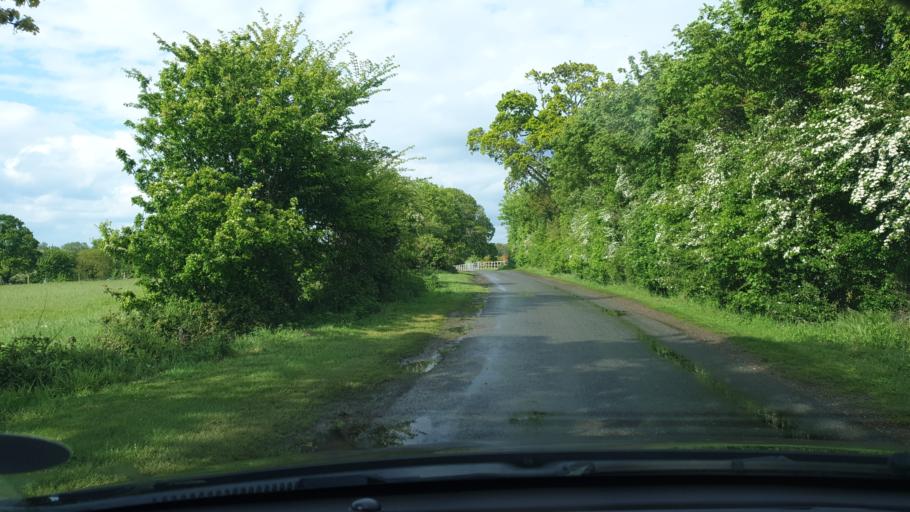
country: GB
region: England
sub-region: Essex
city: Saint Osyth
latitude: 51.8202
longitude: 1.0748
